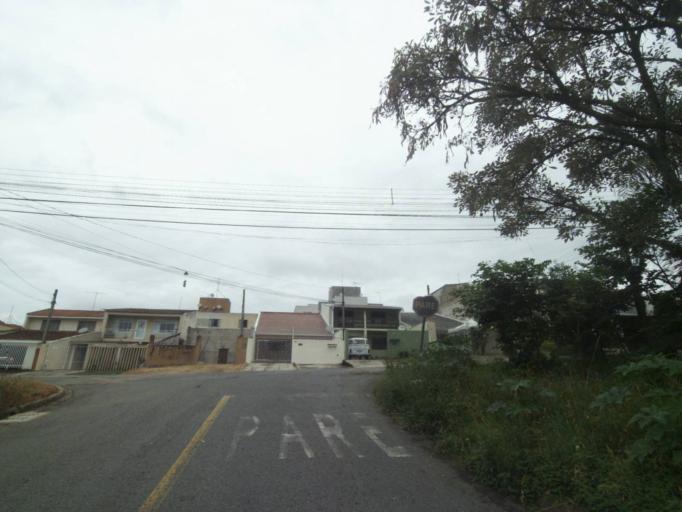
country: BR
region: Parana
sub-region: Curitiba
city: Curitiba
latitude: -25.4572
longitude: -49.3232
